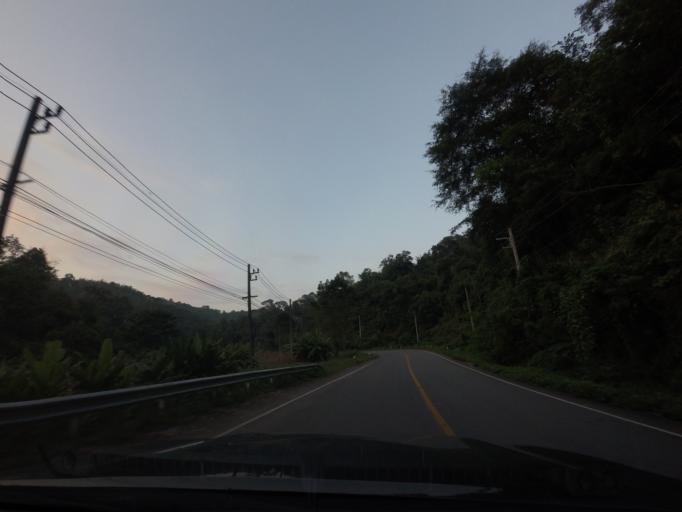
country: TH
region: Nan
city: Na Noi
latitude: 18.4206
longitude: 100.7032
